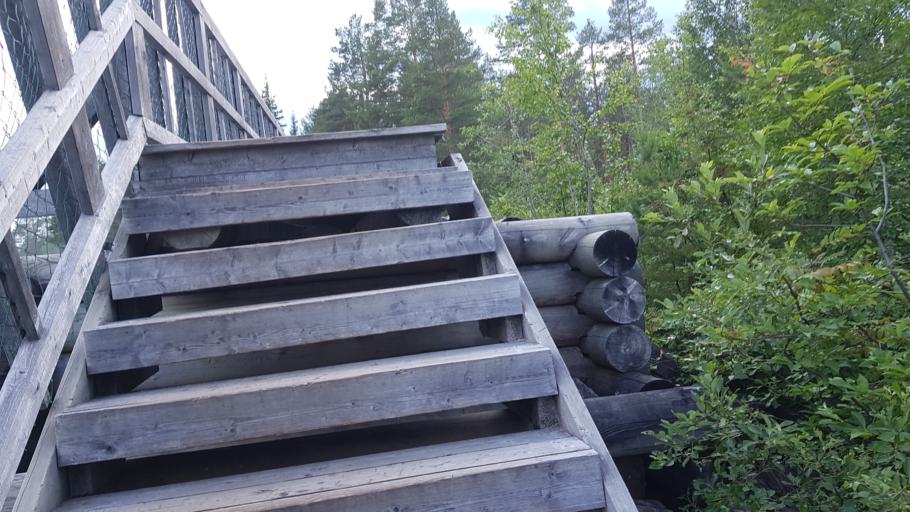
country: SE
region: Norrbotten
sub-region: Alvsbyns Kommun
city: AElvsbyn
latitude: 65.8527
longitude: 20.4108
